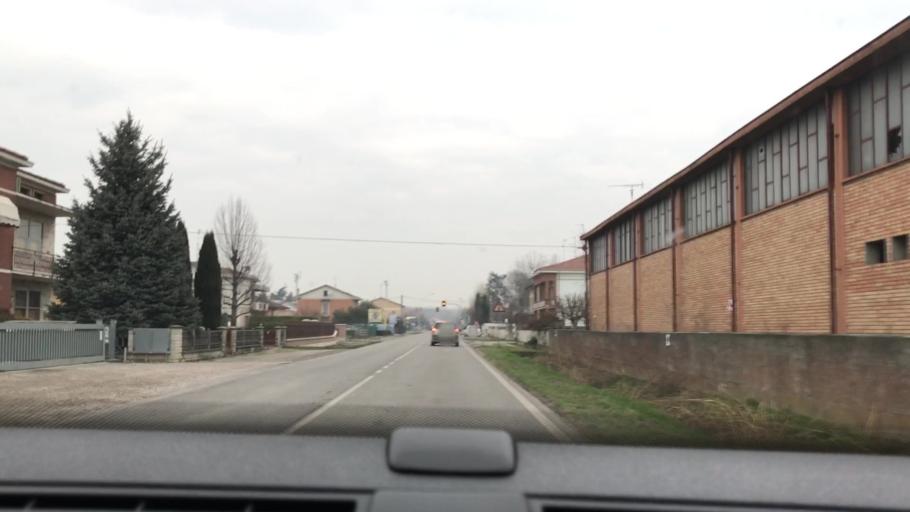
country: IT
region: Lombardy
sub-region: Provincia di Mantova
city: Dosolo
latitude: 44.9505
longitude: 10.6308
